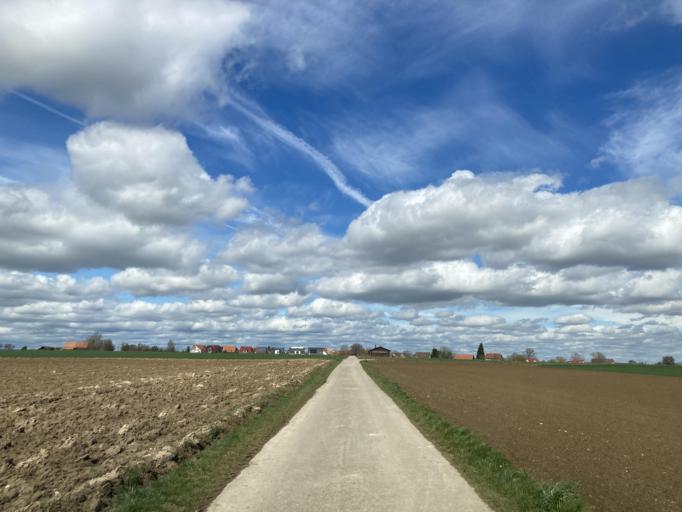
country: DE
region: Baden-Wuerttemberg
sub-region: Regierungsbezirk Stuttgart
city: Bondorf
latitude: 48.4662
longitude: 8.8201
